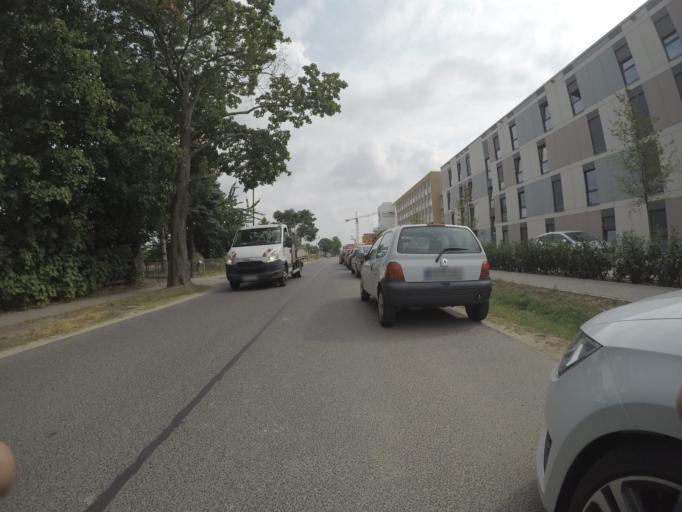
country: DE
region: Brandenburg
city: Schonefeld
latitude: 52.3941
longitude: 13.5018
